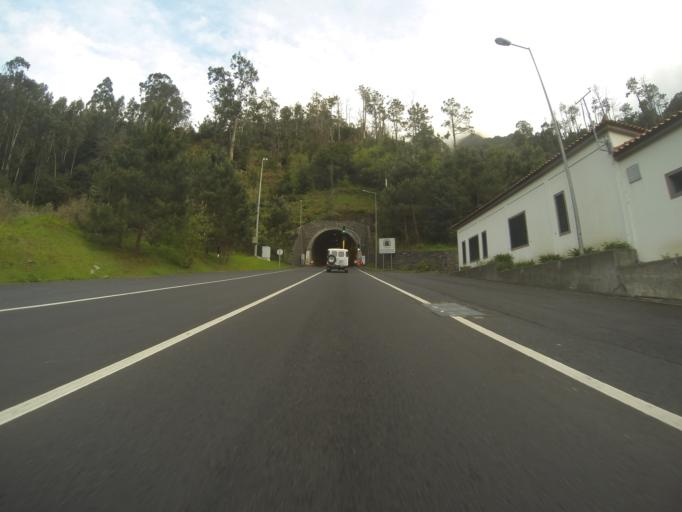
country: PT
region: Madeira
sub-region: Sao Vicente
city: Sao Vicente
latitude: 32.7670
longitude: -17.0296
